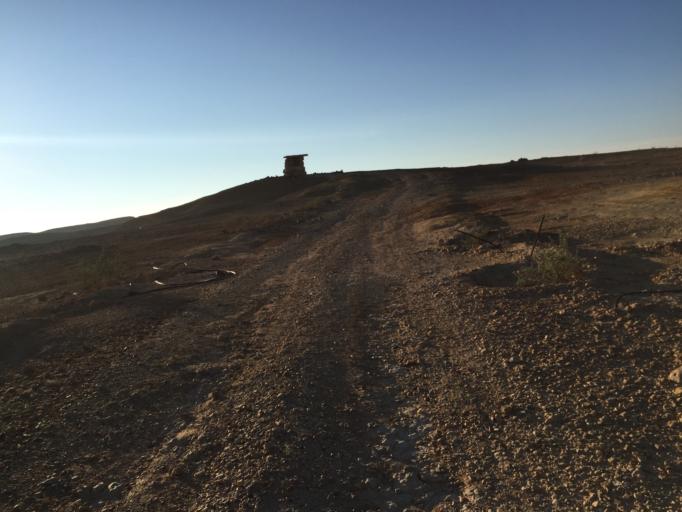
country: IL
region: Southern District
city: Mitzpe Ramon
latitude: 30.5292
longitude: 34.9203
